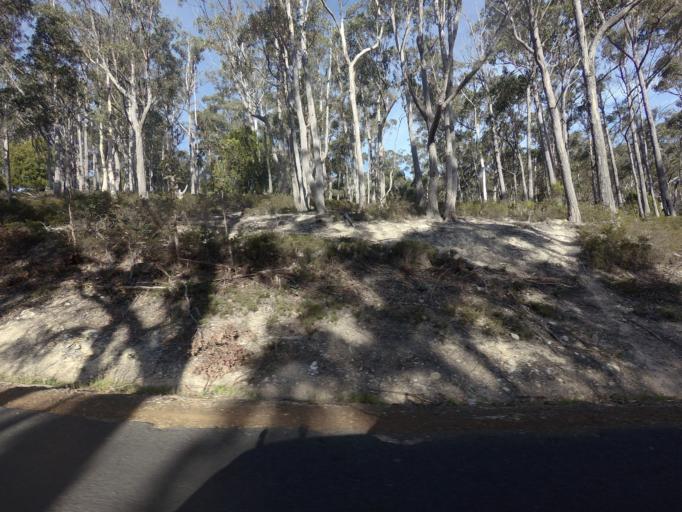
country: AU
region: Tasmania
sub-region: Sorell
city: Sorell
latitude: -42.4850
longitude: 147.4503
